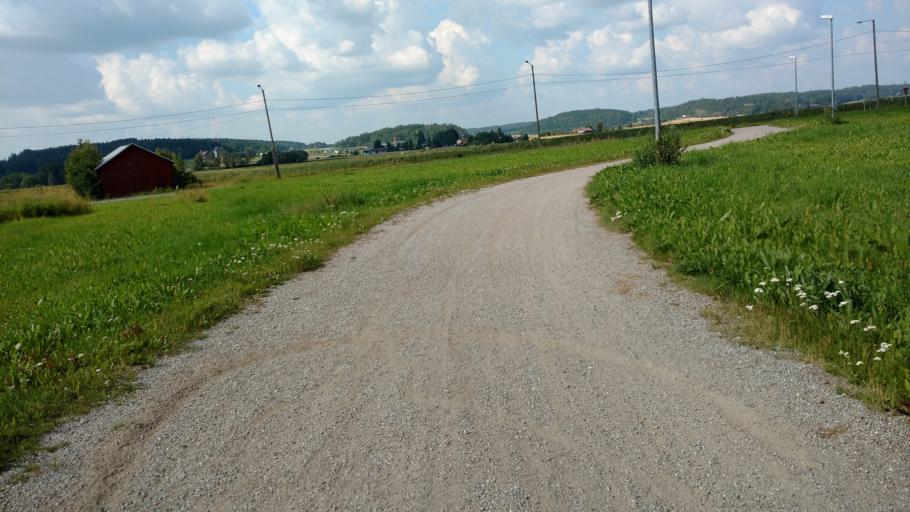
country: FI
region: Varsinais-Suomi
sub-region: Salo
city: Salo
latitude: 60.4068
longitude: 23.1751
